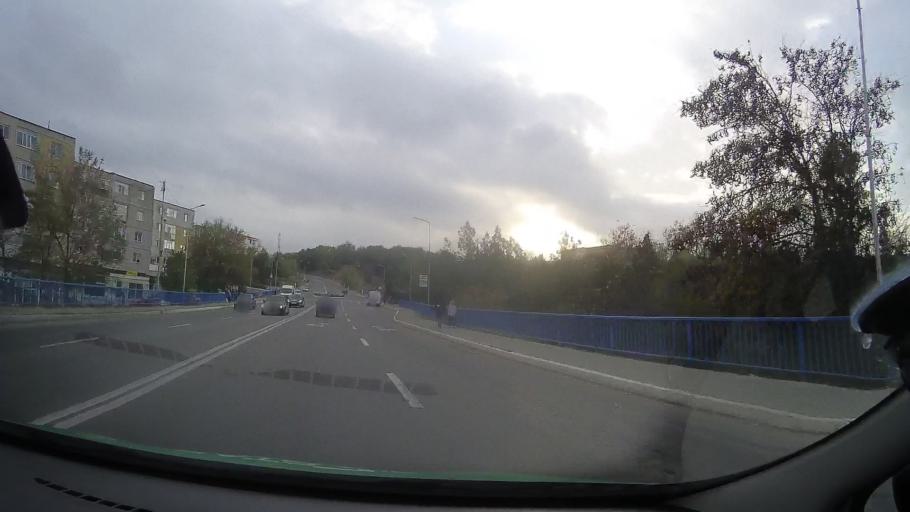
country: RO
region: Constanta
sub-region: Municipiul Medgidia
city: Medgidia
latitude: 44.2479
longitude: 28.2607
